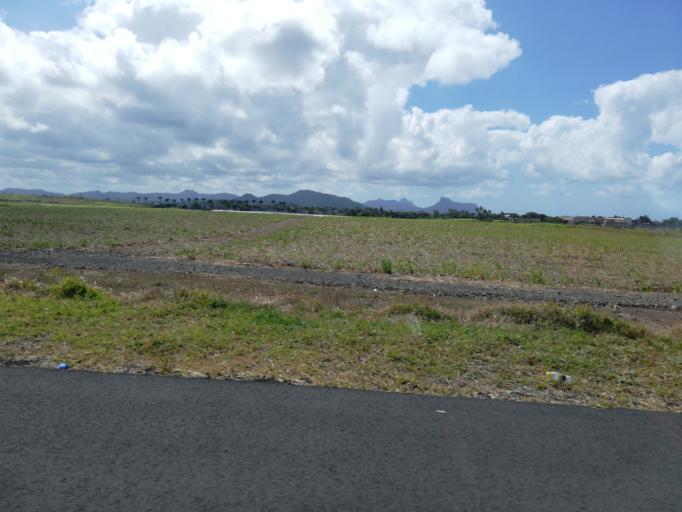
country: MU
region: Grand Port
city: Plaine Magnien
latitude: -20.4375
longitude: 57.6530
